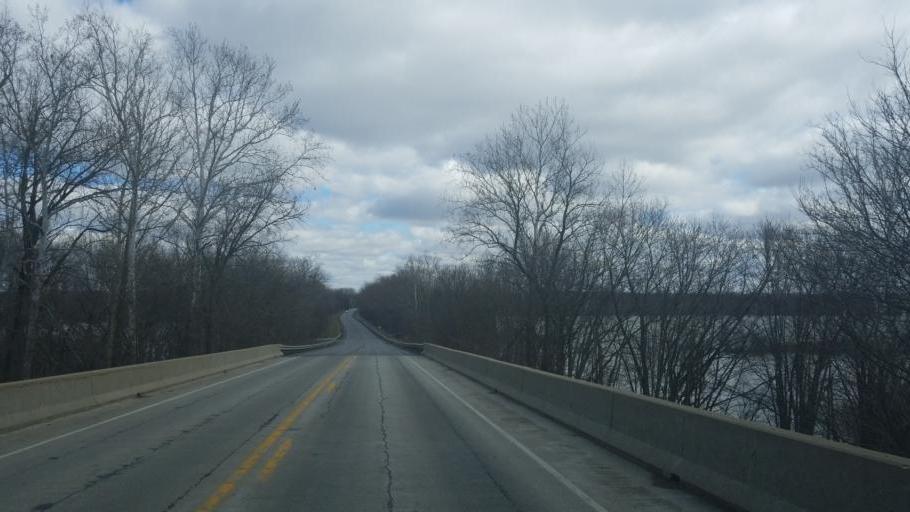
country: US
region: Indiana
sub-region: Parke County
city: Montezuma
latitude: 39.7908
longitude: -87.3865
